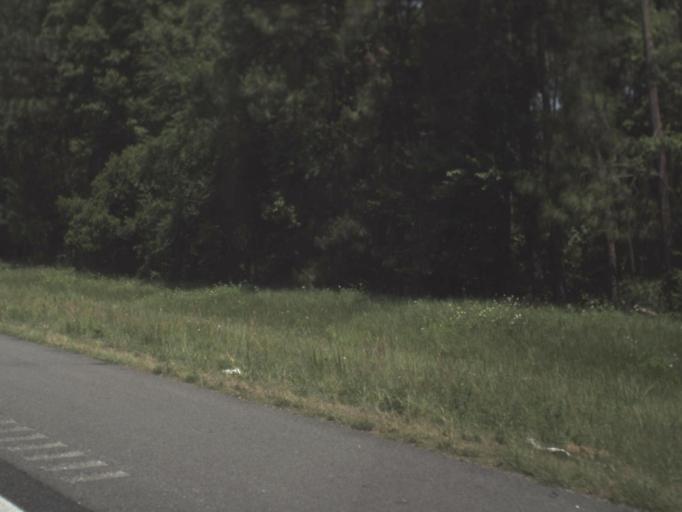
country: US
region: Florida
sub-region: Duval County
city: Baldwin
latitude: 30.3023
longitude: -81.9206
